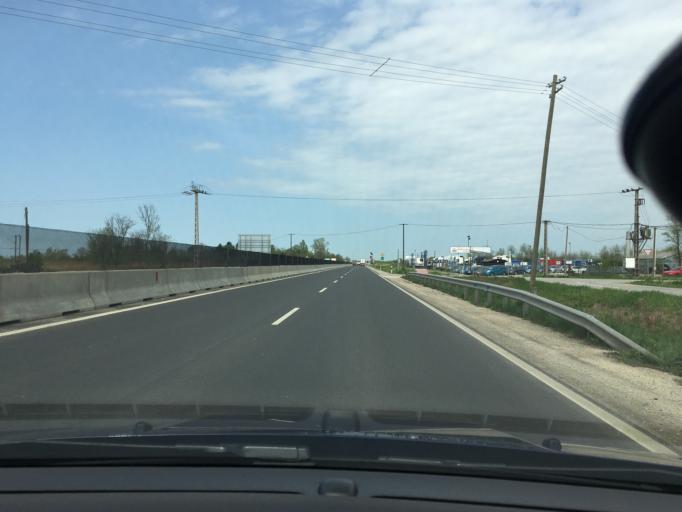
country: HU
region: Csongrad
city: Algyo
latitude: 46.2976
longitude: 20.1782
